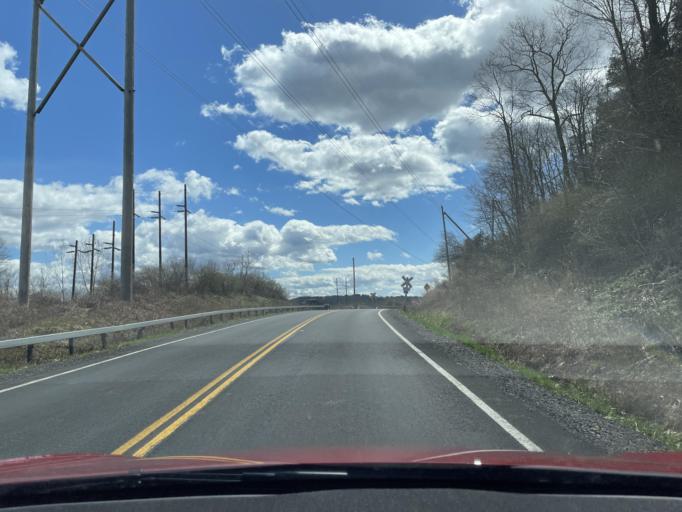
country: US
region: New York
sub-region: Ulster County
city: Hurley
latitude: 41.9507
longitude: -74.0495
